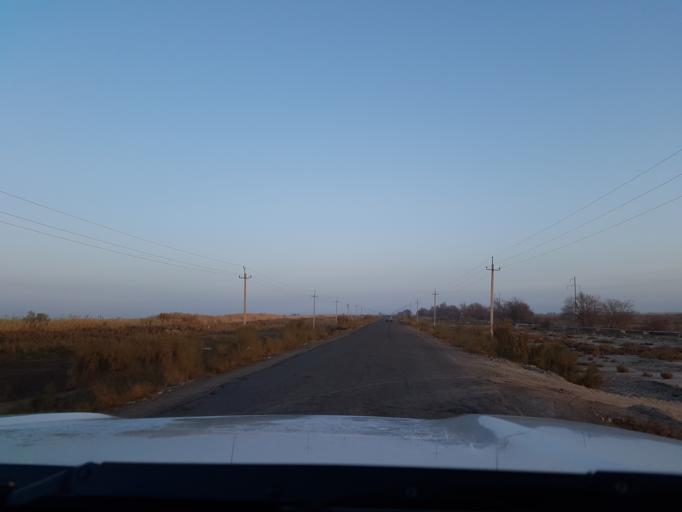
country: TM
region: Dasoguz
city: Koeneuergench
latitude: 41.8258
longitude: 58.7038
